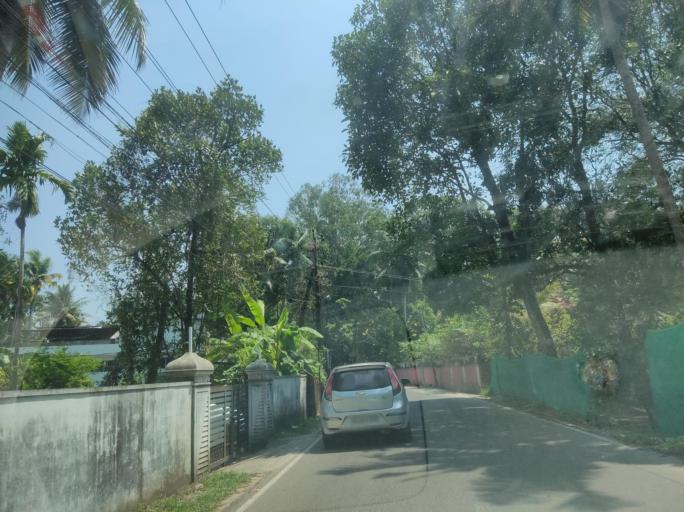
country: IN
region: Kerala
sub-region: Alappuzha
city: Kutiatodu
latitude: 9.8447
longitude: 76.2954
